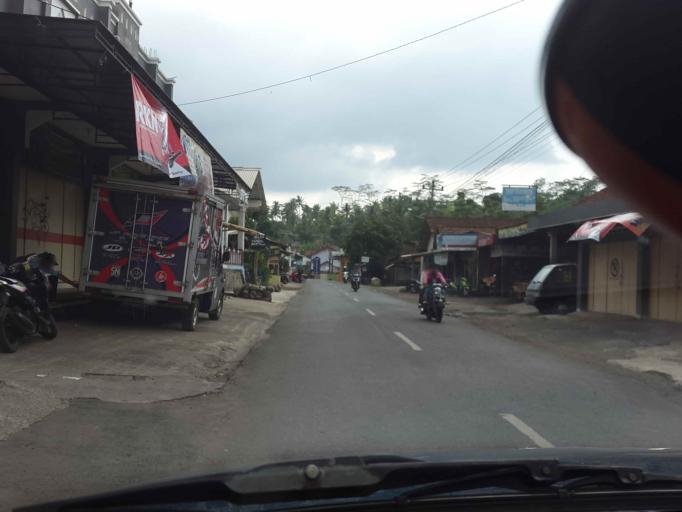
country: ID
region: Central Java
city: Gunung Kendil
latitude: -7.3728
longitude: 110.3253
